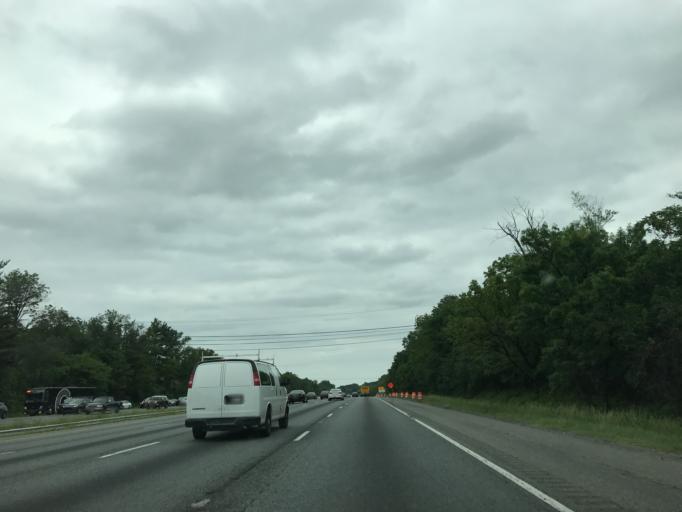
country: US
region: Maryland
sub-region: Howard County
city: West Elkridge
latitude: 39.2085
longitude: -76.7449
